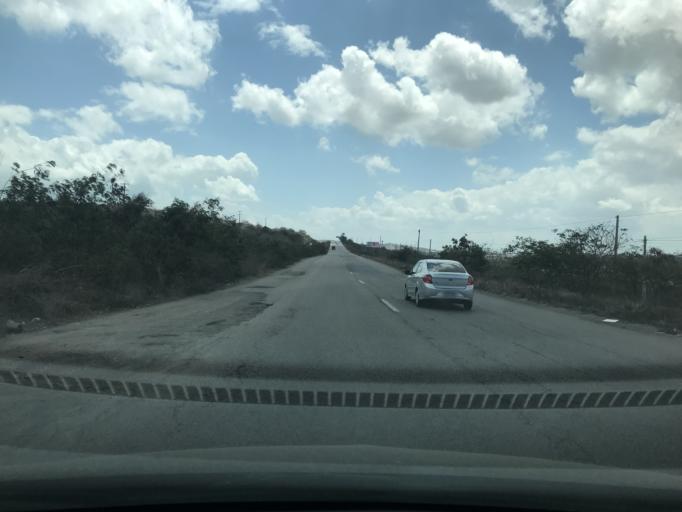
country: BR
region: Pernambuco
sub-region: Caruaru
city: Caruaru
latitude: -8.3055
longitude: -35.9340
